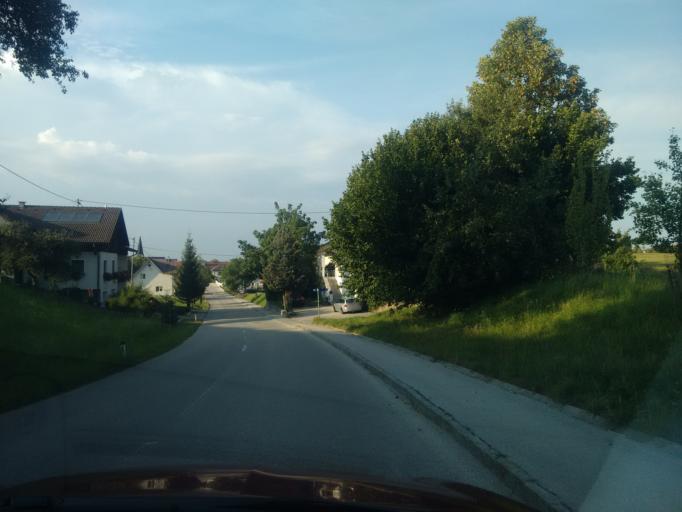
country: AT
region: Upper Austria
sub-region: Politischer Bezirk Vocklabruck
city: Wolfsegg am Hausruck
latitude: 48.1484
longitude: 13.6318
